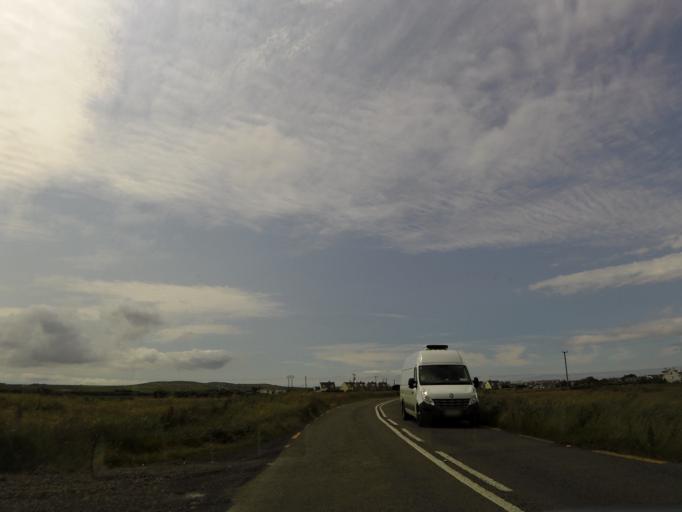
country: IE
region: Munster
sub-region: An Clar
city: Kilrush
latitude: 52.6753
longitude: -9.6284
